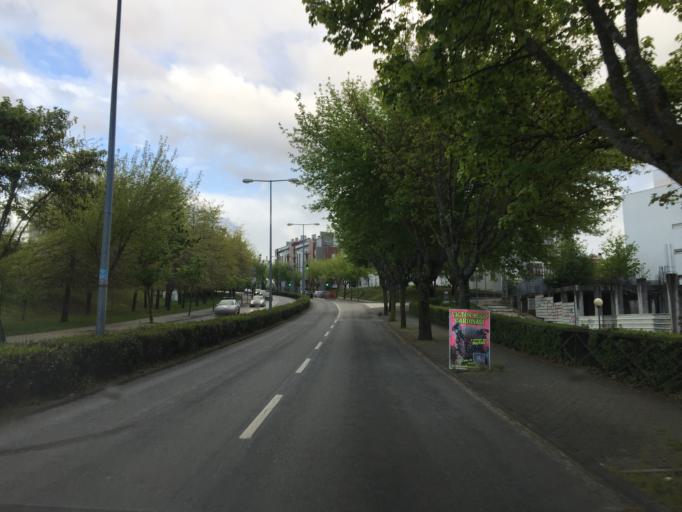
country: PT
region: Viseu
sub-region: Viseu
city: Viseu
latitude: 40.6524
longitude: -7.9217
